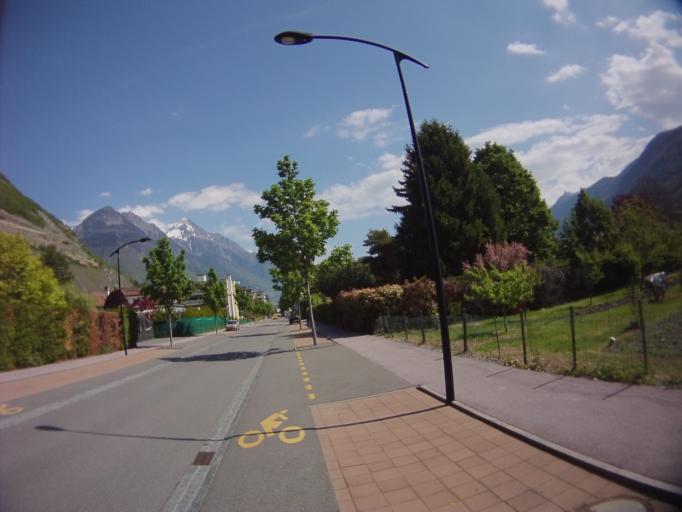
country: CH
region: Valais
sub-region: Martigny District
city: Martigny-Ville
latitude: 46.0960
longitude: 7.0636
